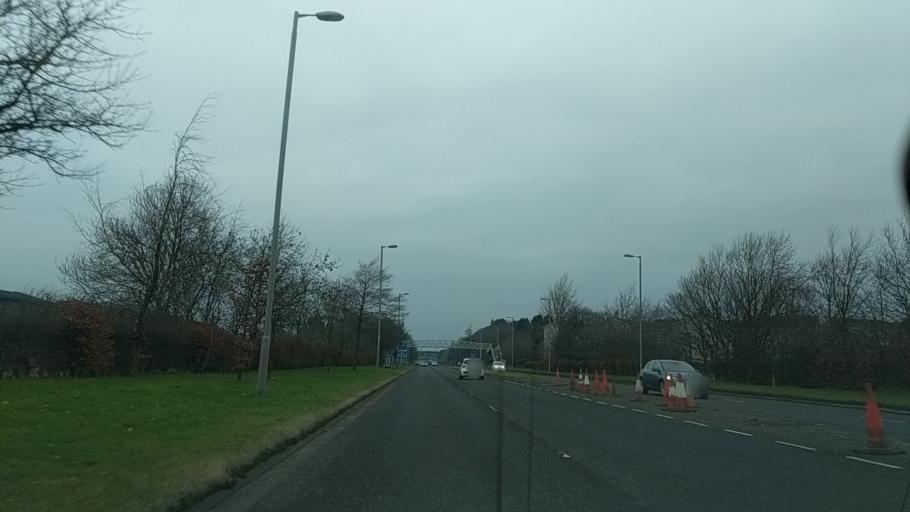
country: GB
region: Scotland
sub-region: South Lanarkshire
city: East Kilbride
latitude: 55.7622
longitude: -4.1965
